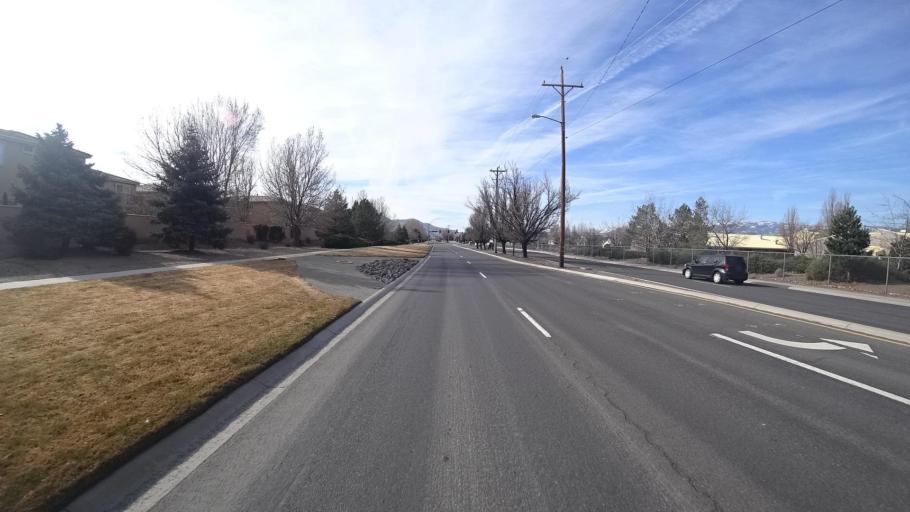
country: US
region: Nevada
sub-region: Washoe County
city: Sparks
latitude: 39.5523
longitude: -119.7056
